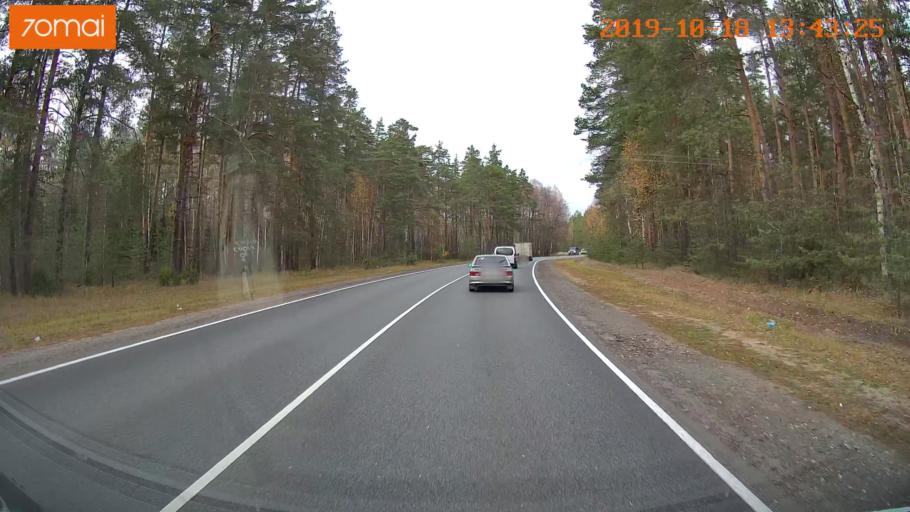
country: RU
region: Rjazan
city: Solotcha
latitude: 54.9301
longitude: 39.9751
